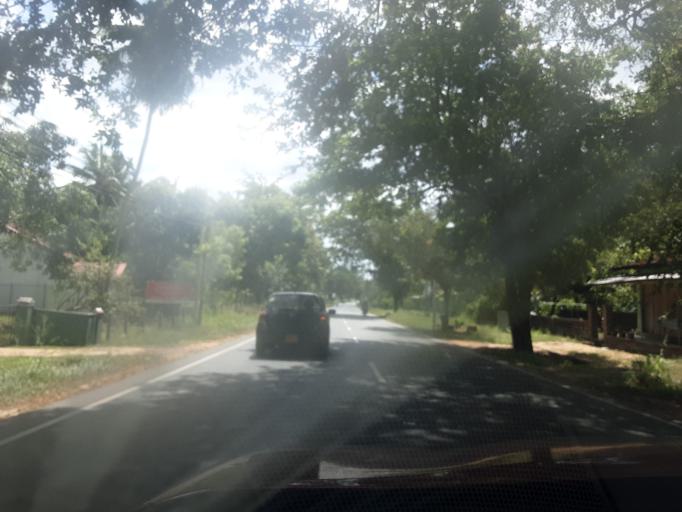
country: LK
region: North Western
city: Kuliyapitiya
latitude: 7.4841
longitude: 79.9782
